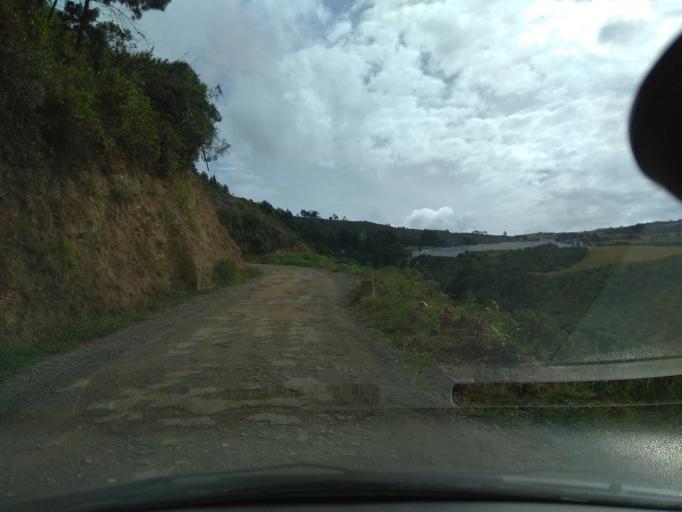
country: CO
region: Boyaca
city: Santa Rosa de Viterbo
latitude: 5.8908
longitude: -72.9733
